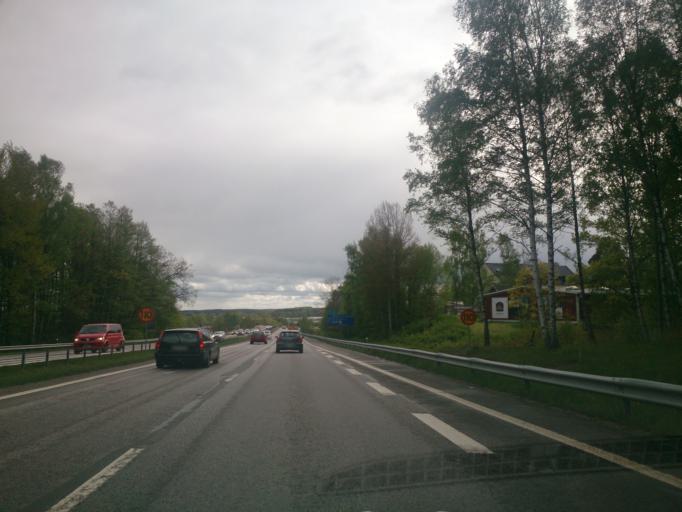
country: SE
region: Soedermanland
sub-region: Nykopings Kommun
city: Nykoping
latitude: 58.7603
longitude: 16.9872
